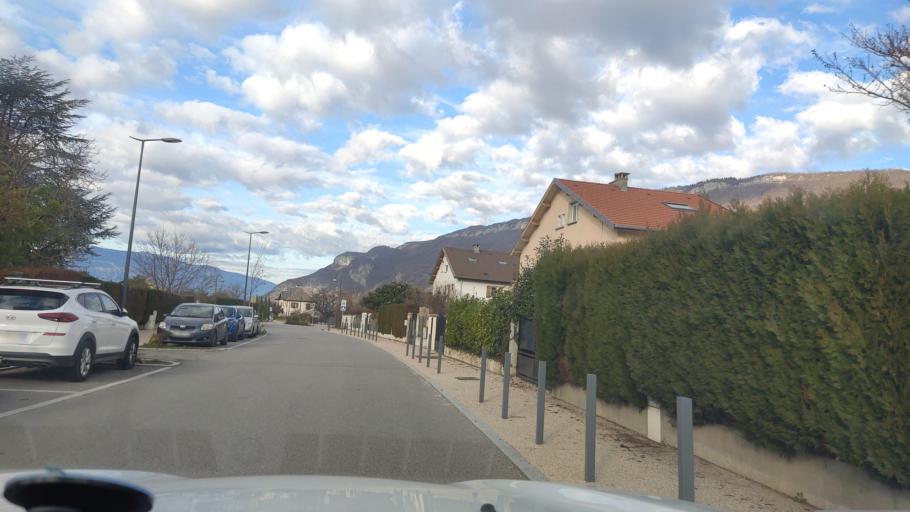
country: FR
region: Rhone-Alpes
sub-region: Departement de la Savoie
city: Brison-Saint-Innocent
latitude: 45.7267
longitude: 5.8878
